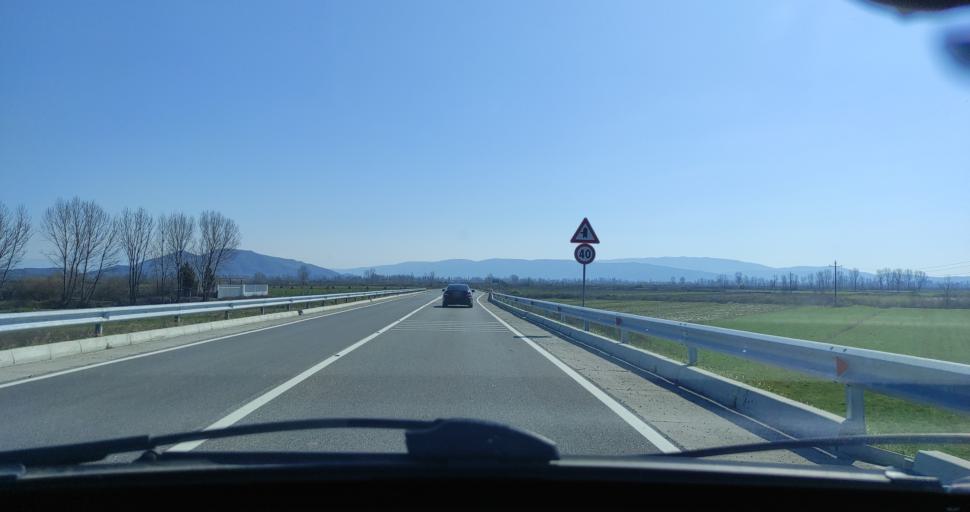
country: AL
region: Shkoder
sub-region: Rrethi i Shkodres
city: Berdica e Madhe
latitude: 42.0075
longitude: 19.4785
